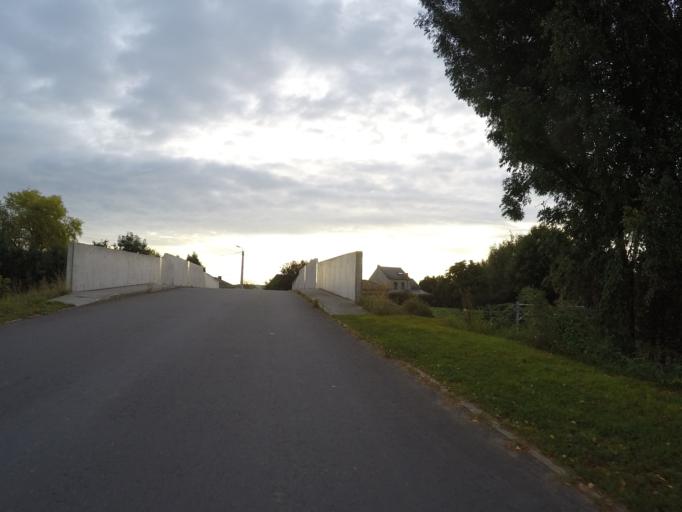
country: BE
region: Wallonia
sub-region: Province de Namur
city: Ciney
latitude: 50.3332
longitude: 5.0630
